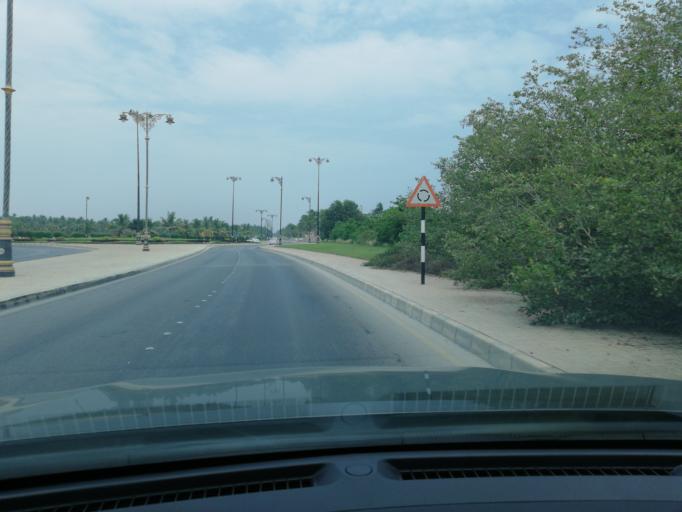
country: OM
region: Zufar
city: Salalah
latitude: 16.9983
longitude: 54.0745
